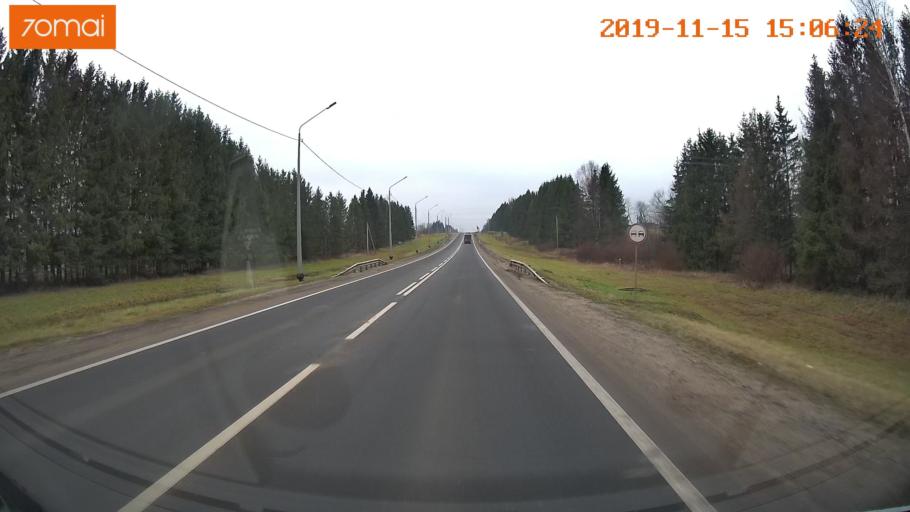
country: RU
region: Jaroslavl
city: Prechistoye
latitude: 58.3927
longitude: 40.3107
